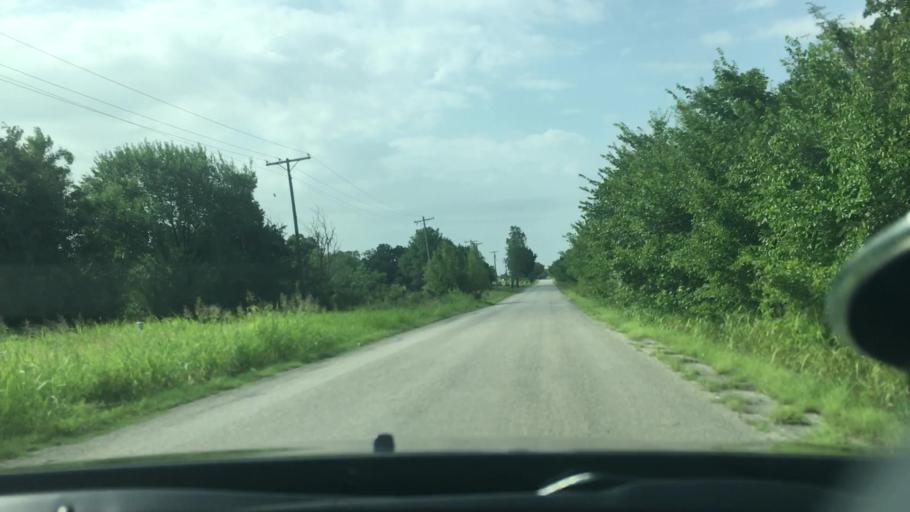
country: US
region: Oklahoma
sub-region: Carter County
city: Lone Grove
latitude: 34.2228
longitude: -97.2737
